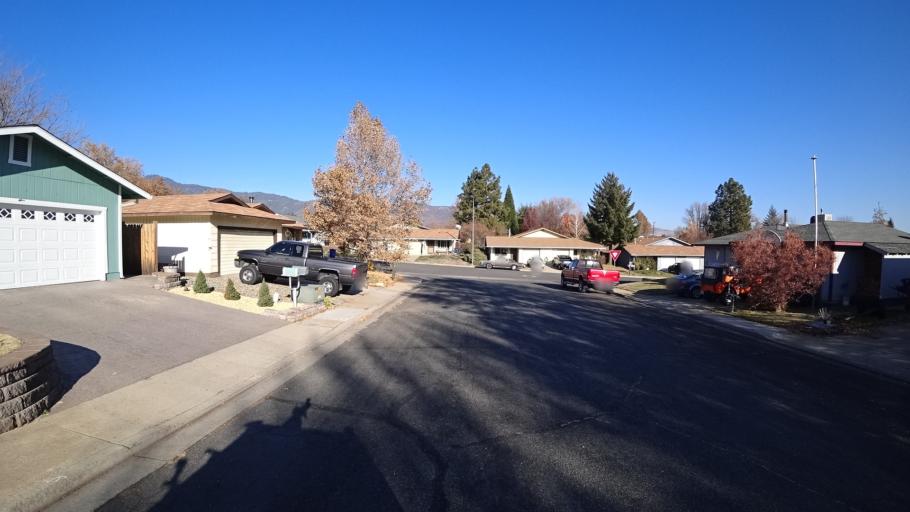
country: US
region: California
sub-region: Siskiyou County
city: Yreka
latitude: 41.7227
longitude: -122.6467
